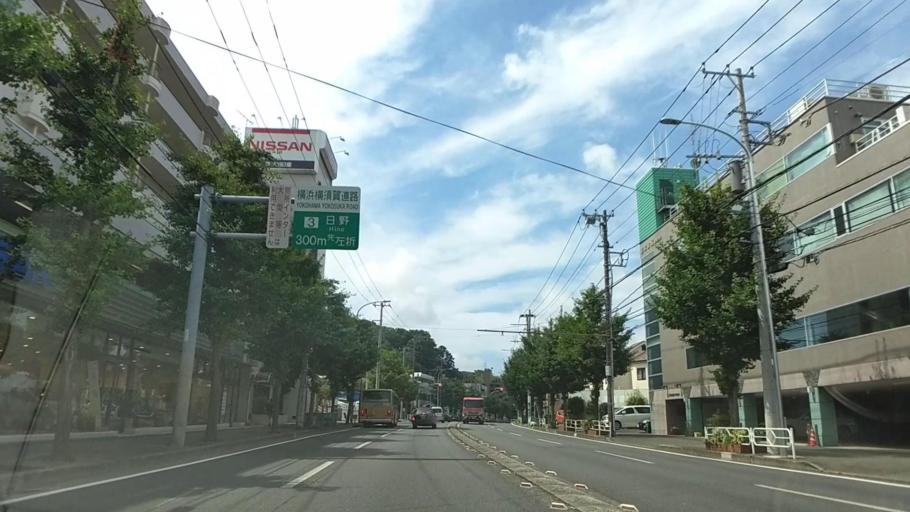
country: JP
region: Kanagawa
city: Yokohama
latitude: 35.3887
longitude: 139.5821
